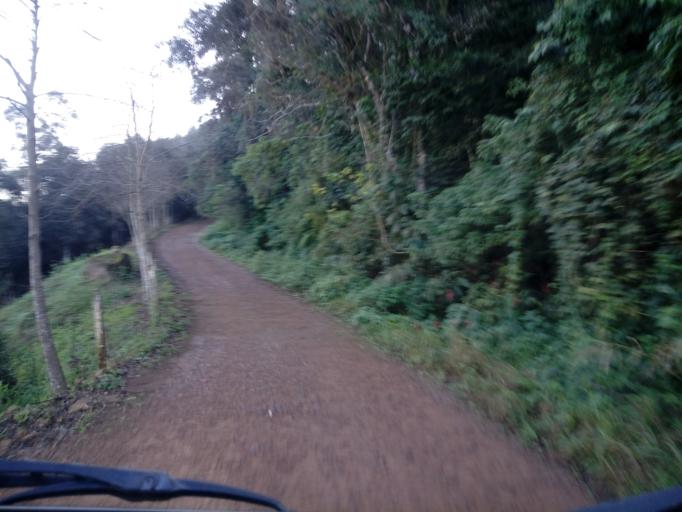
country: BR
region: Santa Catarina
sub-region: Chapeco
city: Chapeco
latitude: -27.2329
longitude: -52.6708
